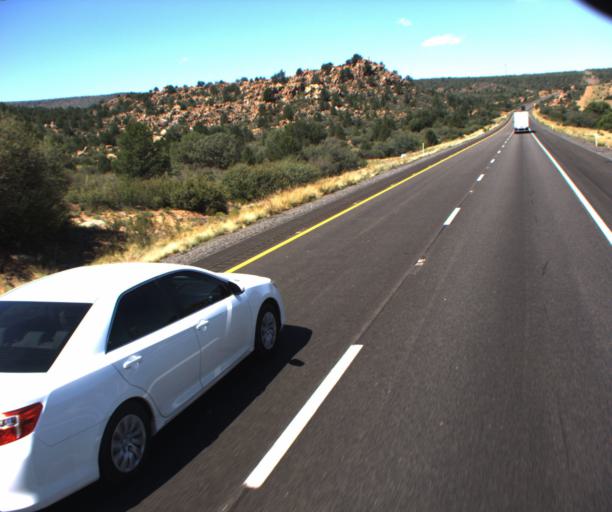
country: US
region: Arizona
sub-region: Mohave County
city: Peach Springs
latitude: 35.1908
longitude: -113.3880
